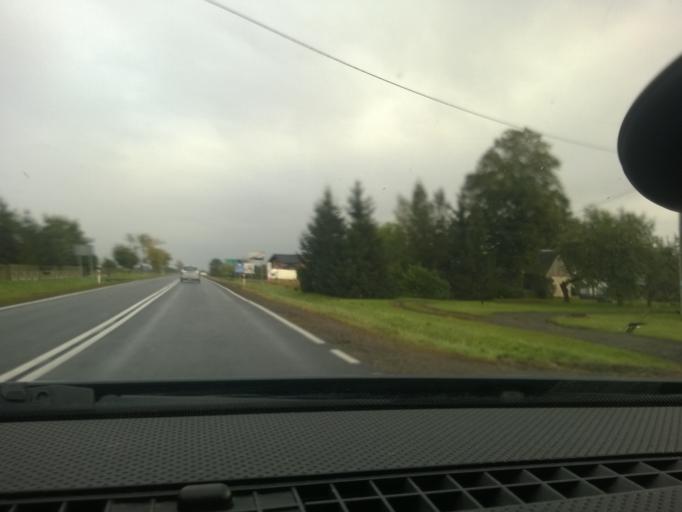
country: PL
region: Lodz Voivodeship
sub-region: Powiat sieradzki
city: Blaszki
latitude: 51.6843
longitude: 18.3320
